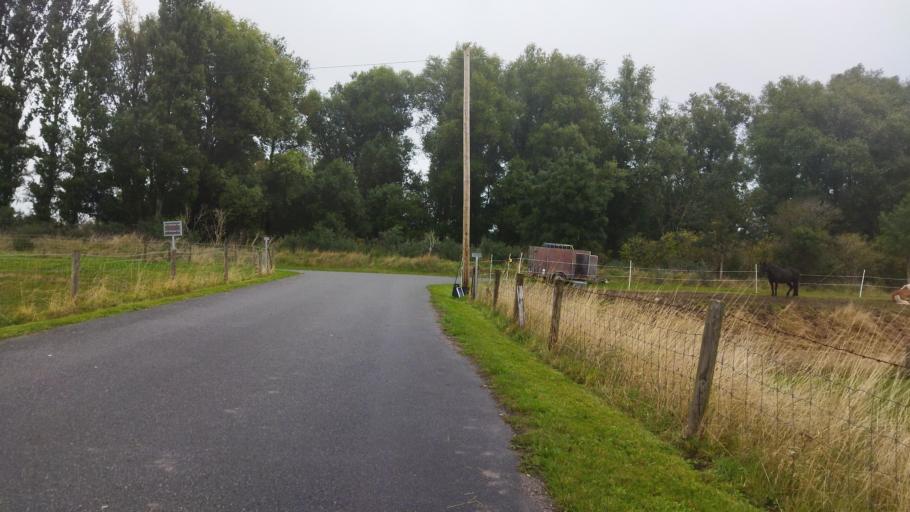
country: NL
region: Groningen
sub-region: Gemeente Delfzijl
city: Delfzijl
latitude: 53.3382
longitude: 7.0545
